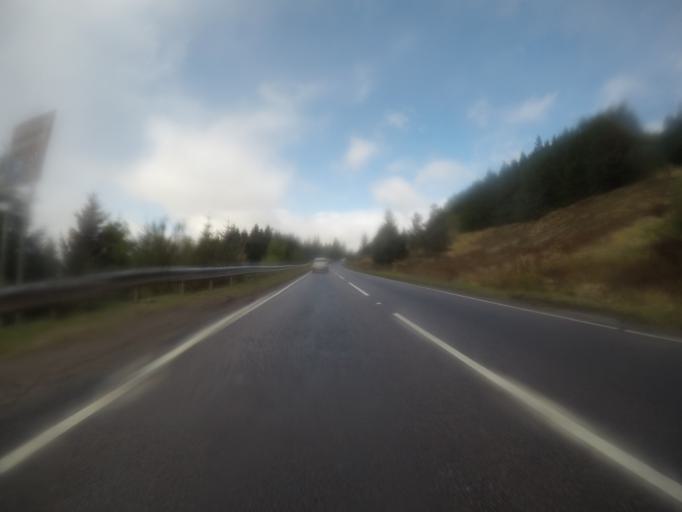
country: GB
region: Scotland
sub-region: Highland
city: Spean Bridge
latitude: 57.0821
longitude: -4.9537
